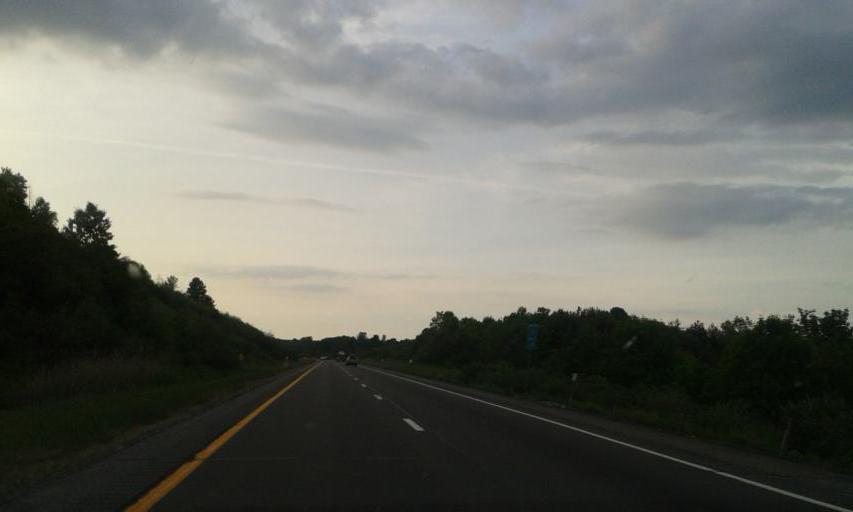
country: US
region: New York
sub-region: Broome County
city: Chenango Bridge
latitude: 42.2646
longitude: -75.9196
